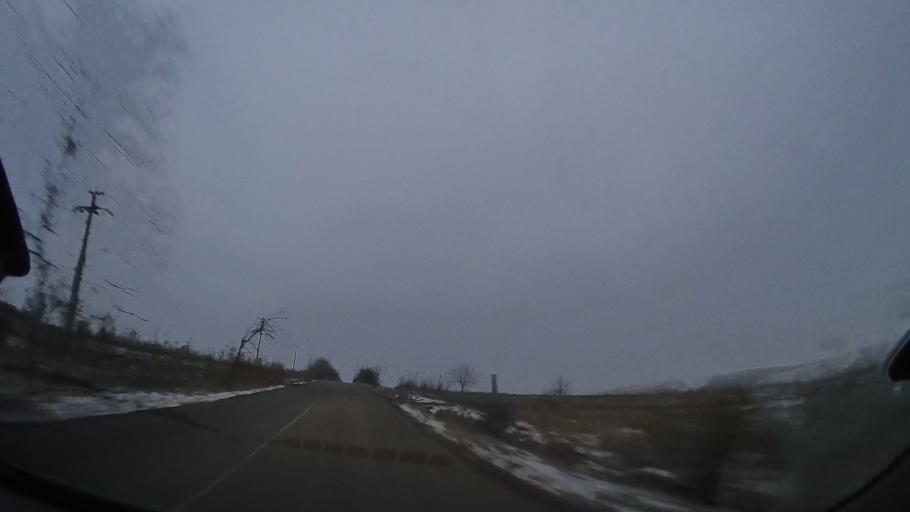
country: RO
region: Vaslui
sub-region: Comuna Gagesti
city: Gagesti
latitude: 46.3957
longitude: 27.9806
